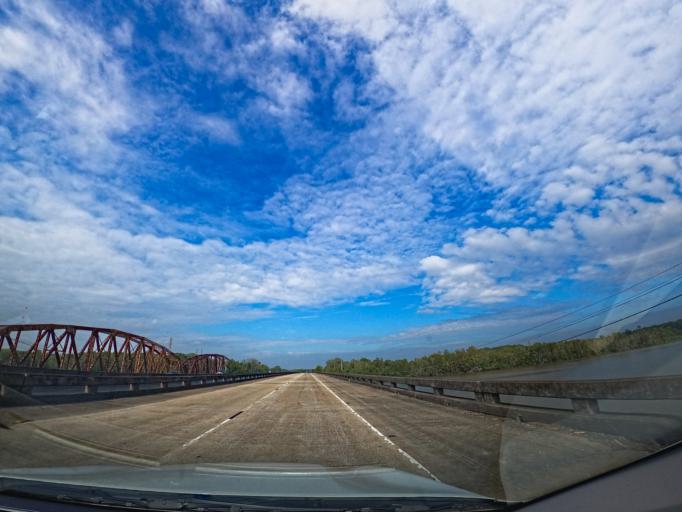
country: US
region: Louisiana
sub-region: Saint Mary Parish
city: Patterson
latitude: 29.6987
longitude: -91.3724
